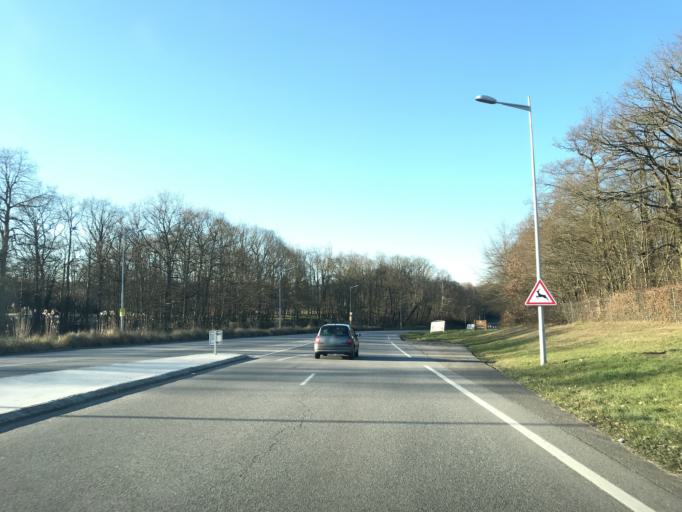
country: FR
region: Haute-Normandie
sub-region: Departement de l'Eure
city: Evreux
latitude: 49.0068
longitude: 1.1446
